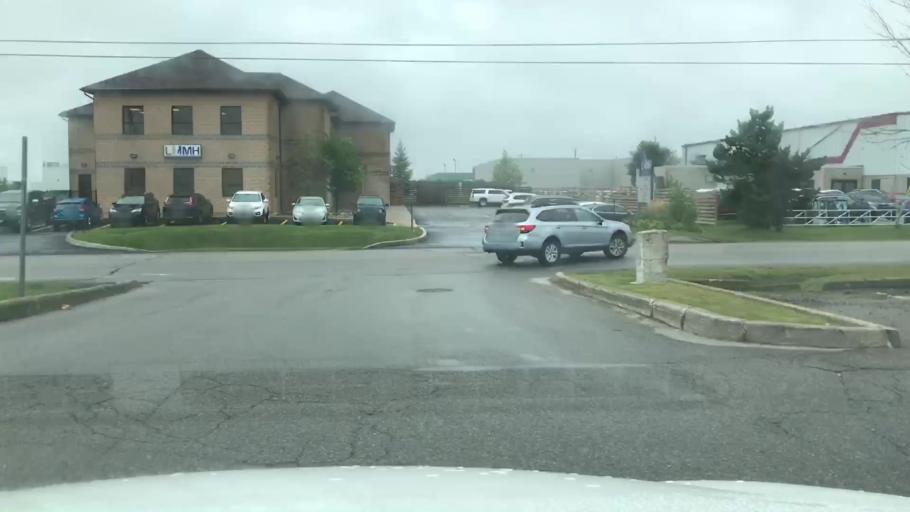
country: CA
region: Ontario
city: Newmarket
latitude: 44.0772
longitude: -79.4276
